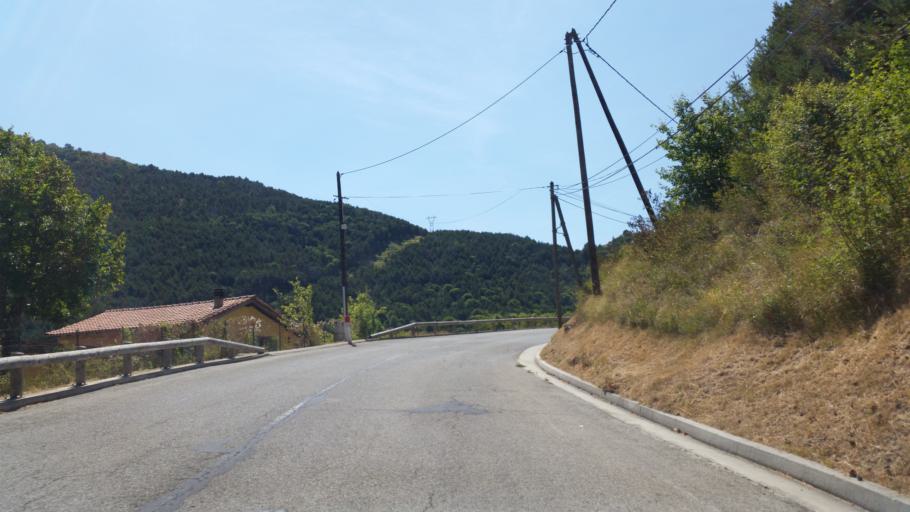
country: FR
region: Provence-Alpes-Cote d'Azur
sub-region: Departement des Alpes-Maritimes
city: Breil-sur-Roya
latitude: 43.9321
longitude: 7.4783
